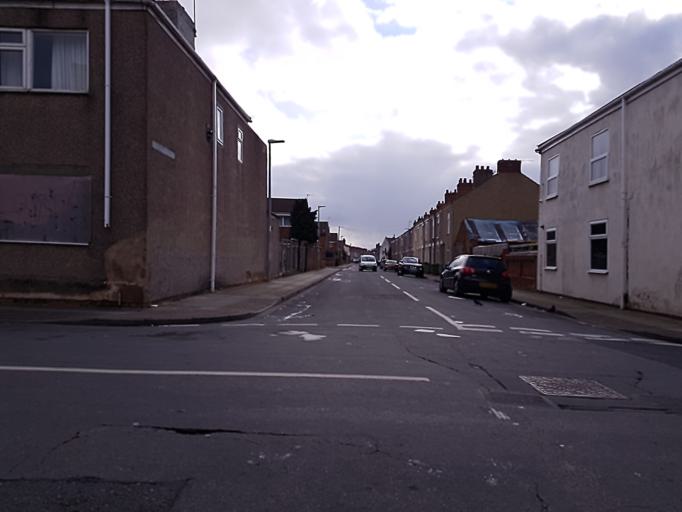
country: GB
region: England
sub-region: North East Lincolnshire
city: Grimsby
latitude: 53.5690
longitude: -0.0616
